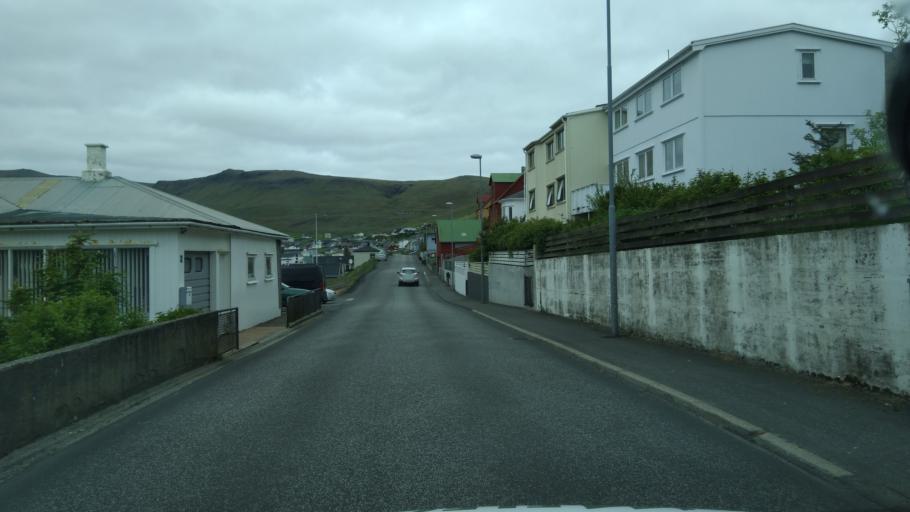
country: FO
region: Suduroy
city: Tvoroyri
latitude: 61.5582
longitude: -6.8209
